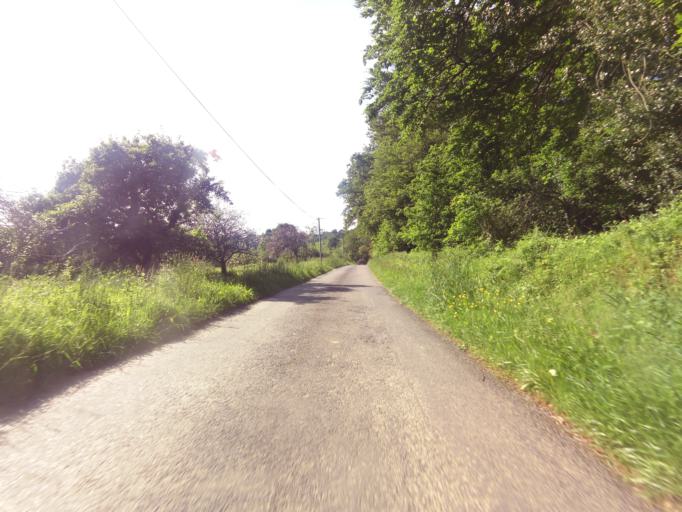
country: FR
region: Brittany
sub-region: Departement du Morbihan
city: Pluherlin
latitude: 47.7134
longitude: -2.3875
